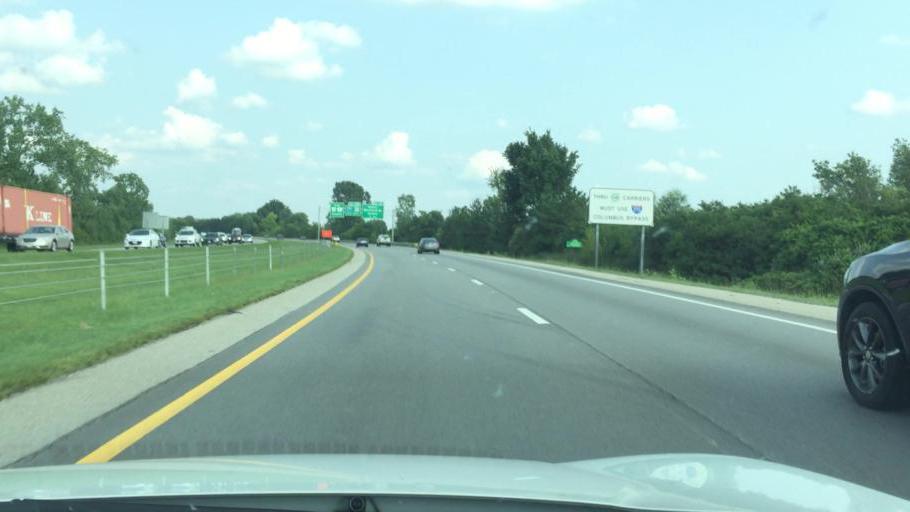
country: US
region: Ohio
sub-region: Franklin County
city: Dublin
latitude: 40.1004
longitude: -83.1720
